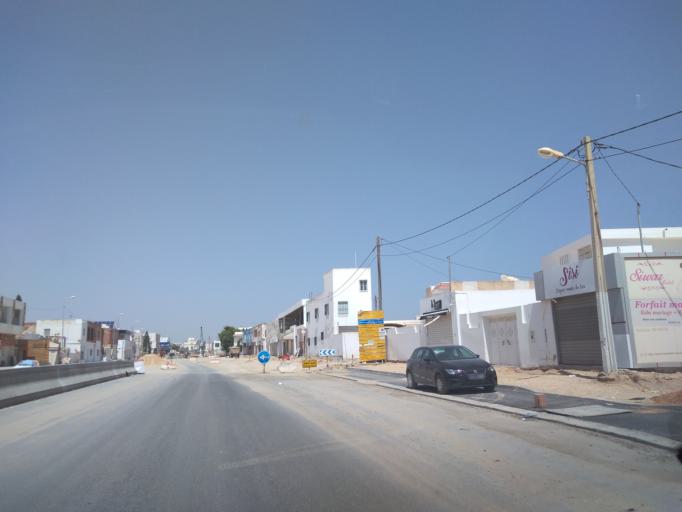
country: TN
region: Safaqis
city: Sfax
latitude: 34.7485
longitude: 10.7282
